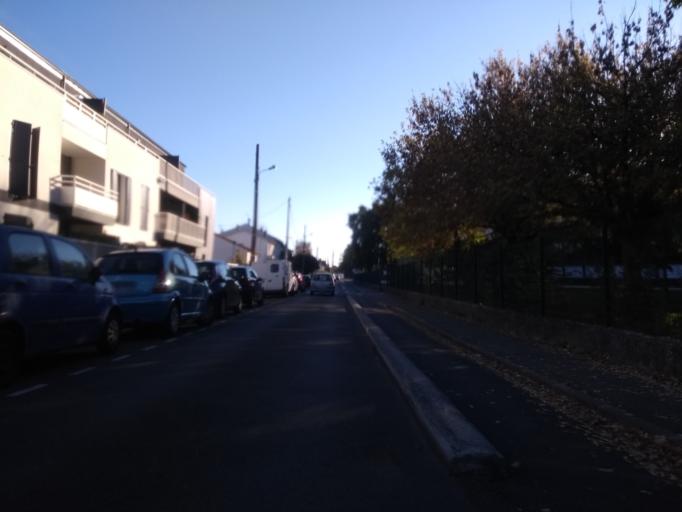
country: FR
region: Aquitaine
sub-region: Departement de la Gironde
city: Talence
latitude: 44.8023
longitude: -0.5896
